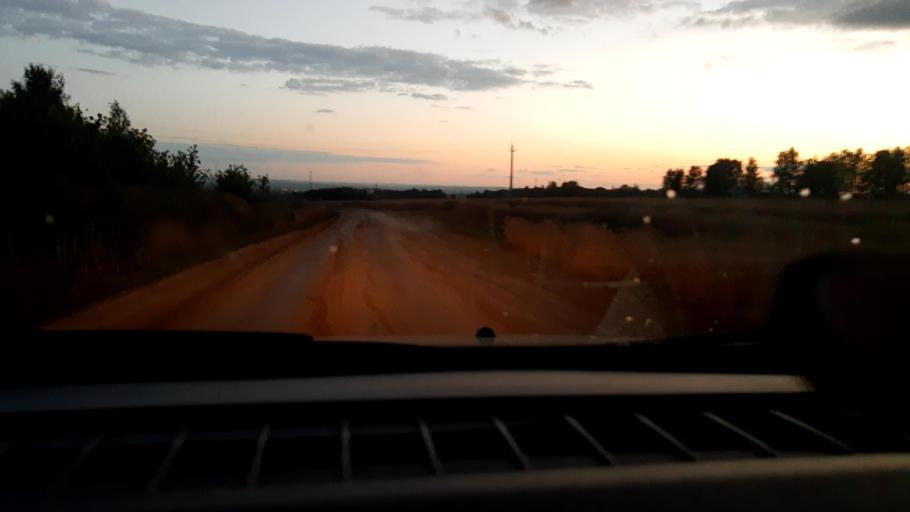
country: RU
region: Nizjnij Novgorod
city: Nizhniy Novgorod
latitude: 56.2048
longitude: 43.9668
